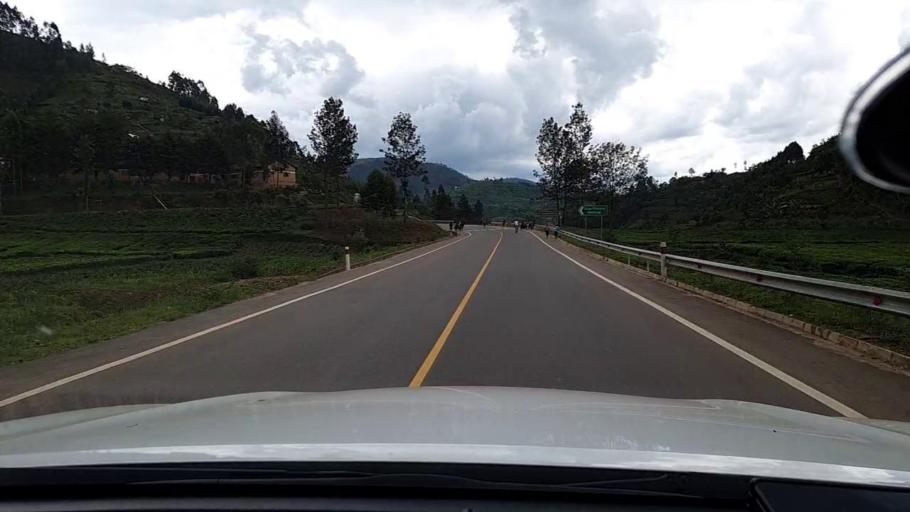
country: RW
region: Northern Province
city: Byumba
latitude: -1.6541
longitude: 29.9117
